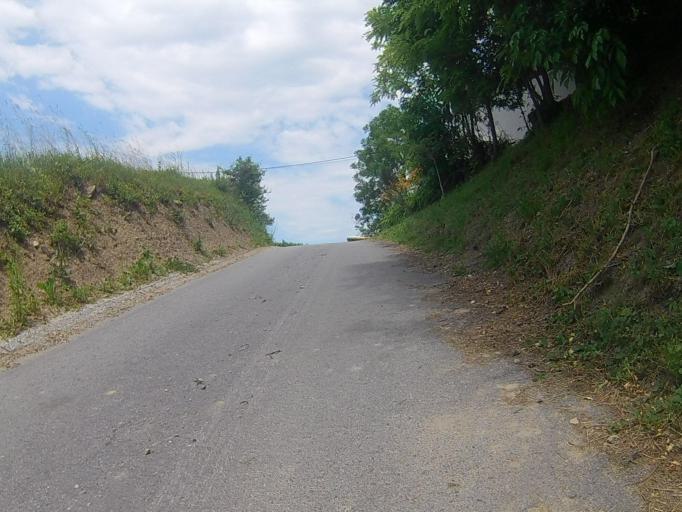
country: SI
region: Maribor
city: Kamnica
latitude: 46.5976
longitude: 15.6314
